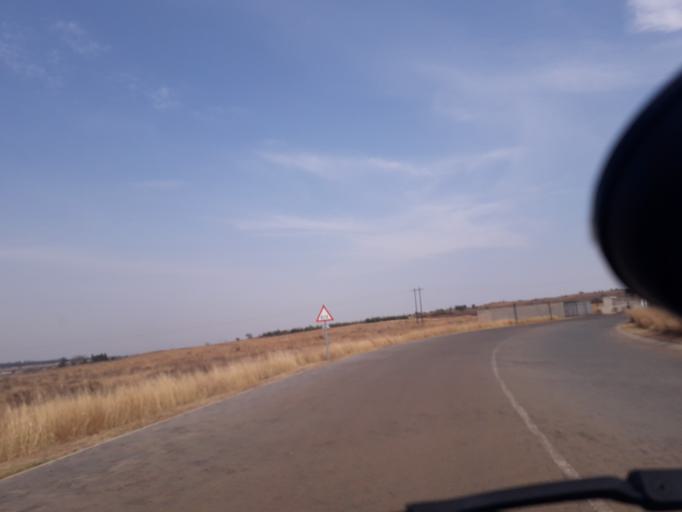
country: ZA
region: Gauteng
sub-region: West Rand District Municipality
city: Krugersdorp
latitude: -25.9765
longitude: 27.6638
